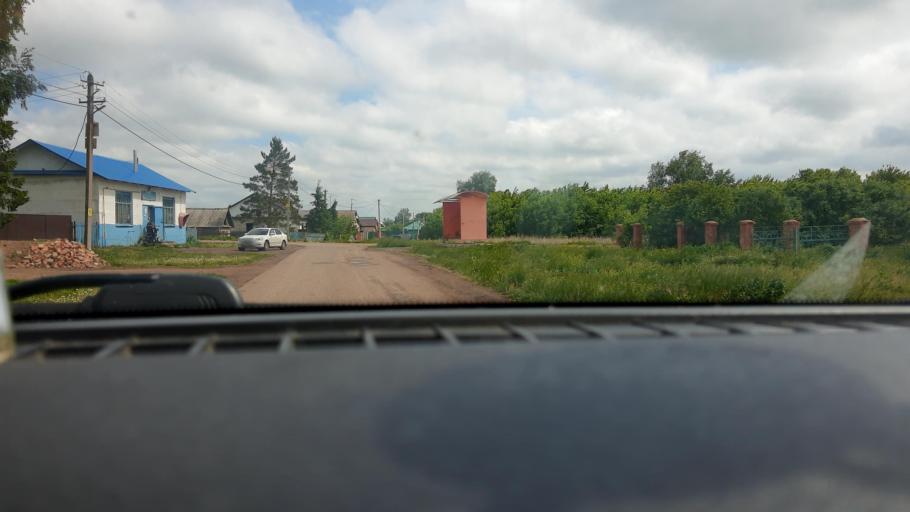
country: RU
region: Bashkortostan
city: Dmitriyevka
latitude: 54.7242
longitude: 55.4981
